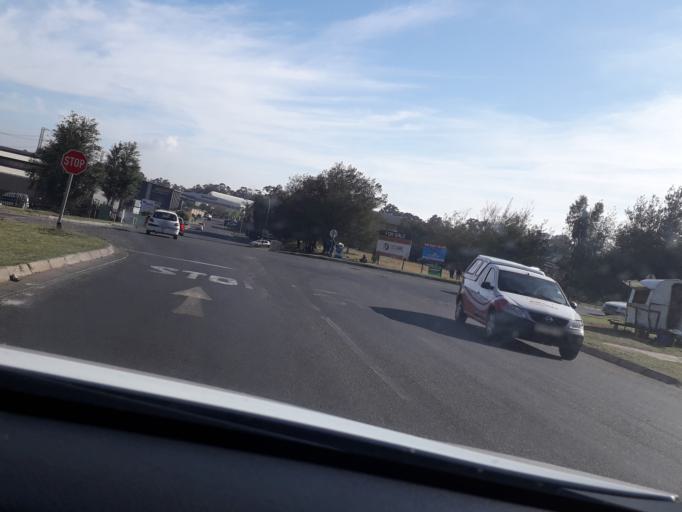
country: ZA
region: Gauteng
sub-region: Ekurhuleni Metropolitan Municipality
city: Germiston
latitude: -26.1613
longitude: 28.1823
